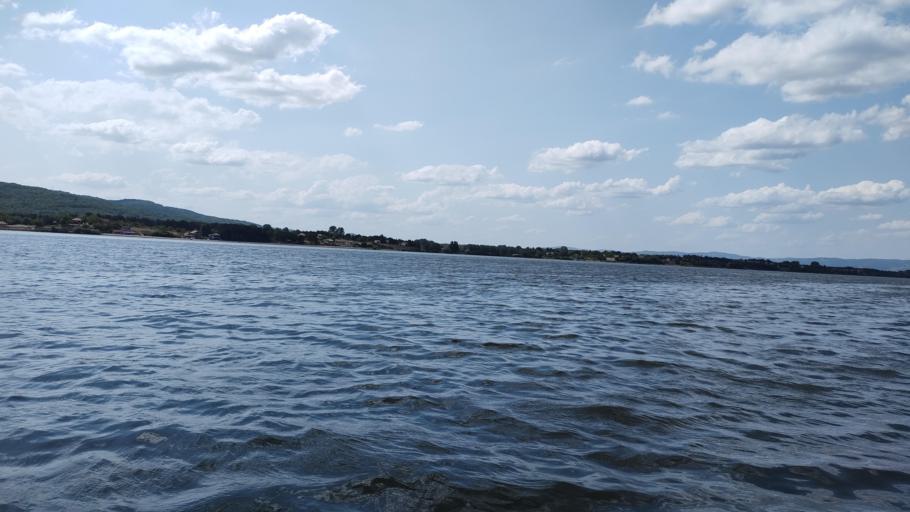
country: RS
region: Central Serbia
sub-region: Branicevski Okrug
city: Golubac
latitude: 44.6765
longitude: 21.6175
